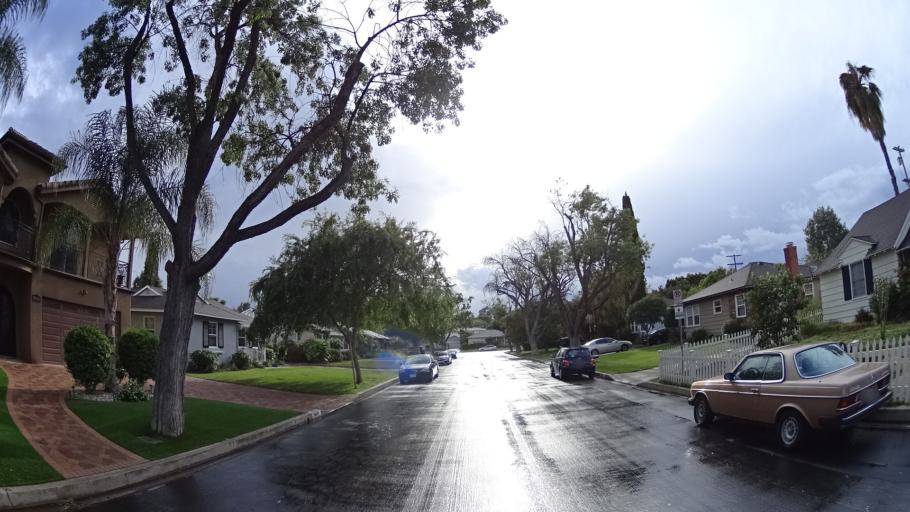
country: US
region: California
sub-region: Los Angeles County
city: Sherman Oaks
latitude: 34.1605
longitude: -118.4380
